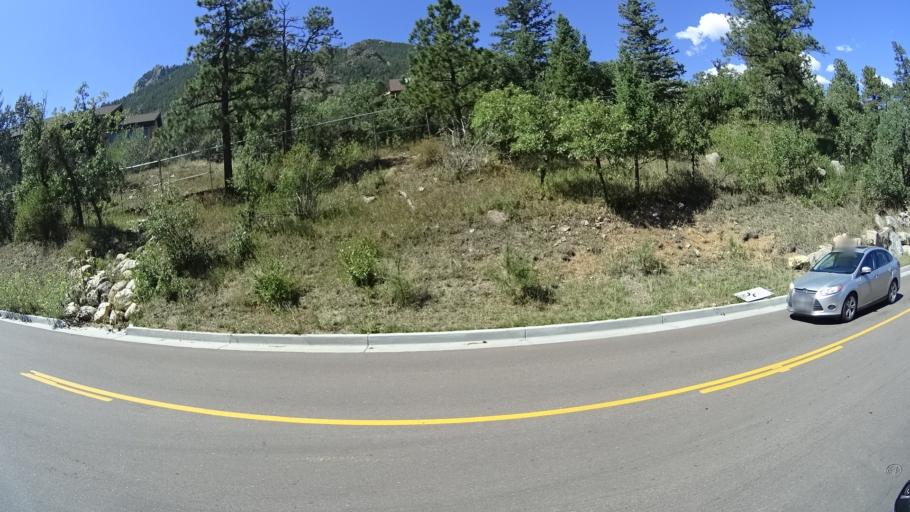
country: US
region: Colorado
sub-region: El Paso County
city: Colorado Springs
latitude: 38.7724
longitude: -104.8531
